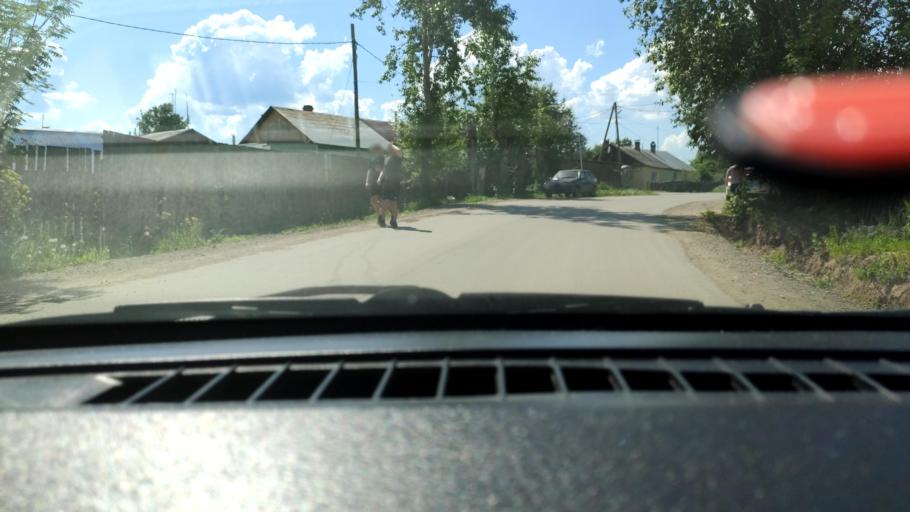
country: RU
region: Perm
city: Sylva
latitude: 58.0325
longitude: 56.7740
